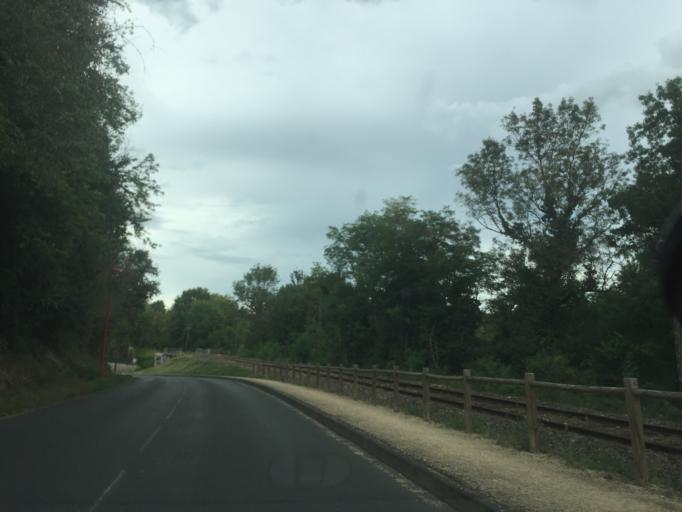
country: FR
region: Aquitaine
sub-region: Departement du Lot-et-Garonne
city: Monsempron-Libos
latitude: 44.4915
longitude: 0.9451
